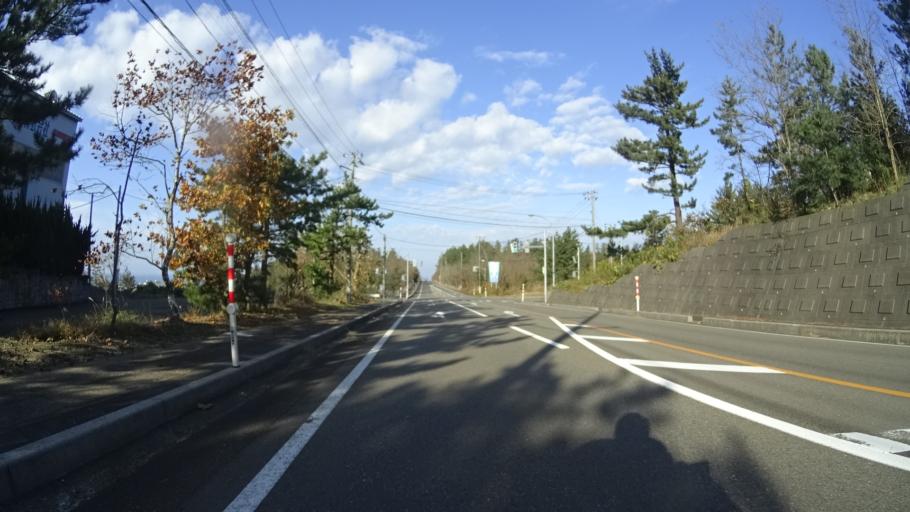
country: JP
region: Niigata
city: Kashiwazaki
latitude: 37.2835
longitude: 138.3987
